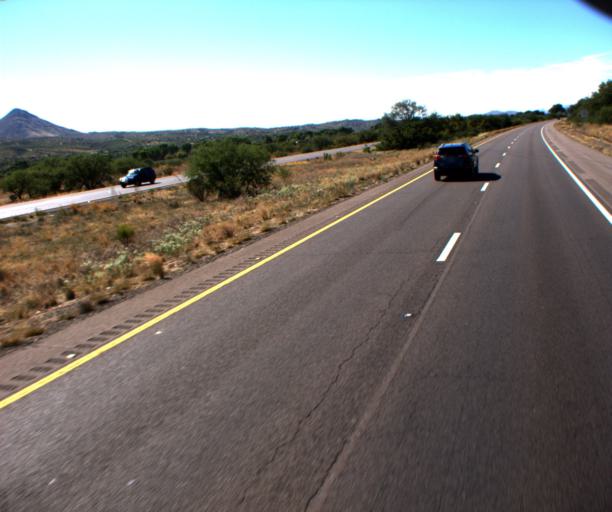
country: US
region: Arizona
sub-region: Santa Cruz County
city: Rio Rico
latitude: 31.5214
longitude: -111.0190
